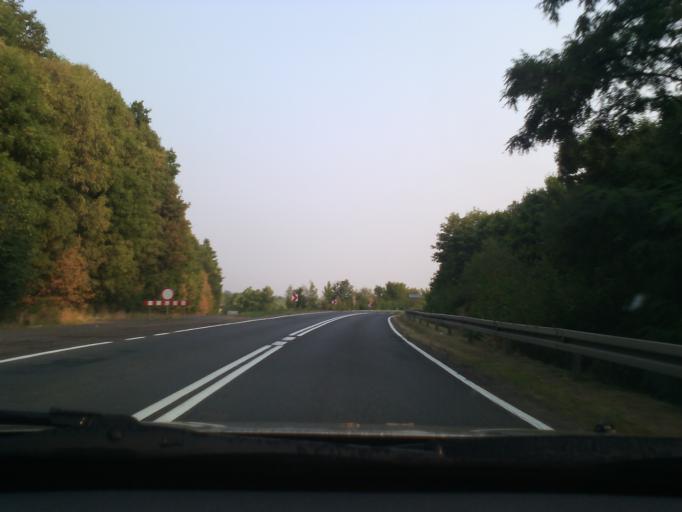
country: PL
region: Lower Silesian Voivodeship
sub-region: Powiat walbrzyski
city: Stare Bogaczowice
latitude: 50.9043
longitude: 16.2520
